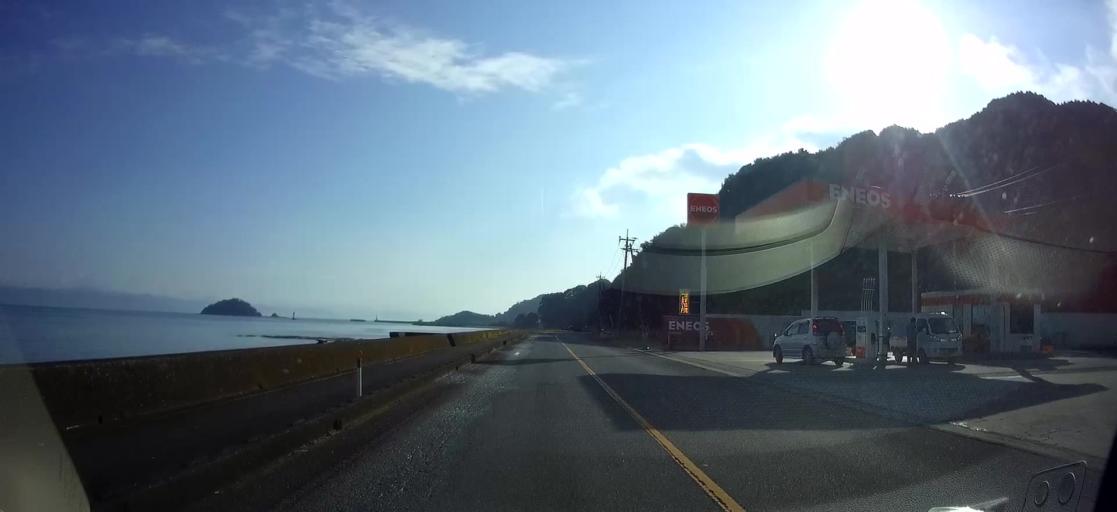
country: JP
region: Kumamoto
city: Yatsushiro
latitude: 32.4815
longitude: 130.4366
